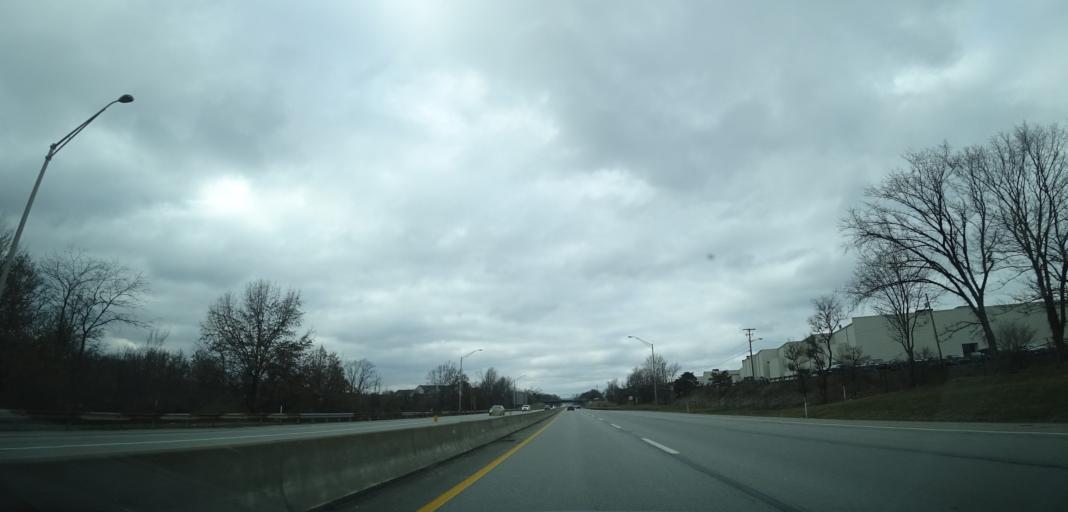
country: US
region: Pennsylvania
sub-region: Butler County
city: Cranberry Township
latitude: 40.6814
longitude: -80.1056
